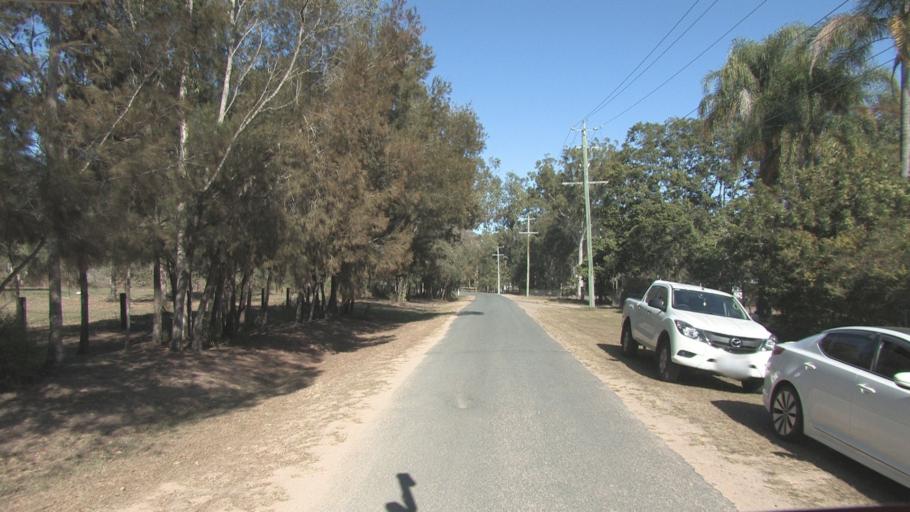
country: AU
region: Queensland
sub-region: Logan
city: Chambers Flat
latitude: -27.7895
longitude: 153.0667
